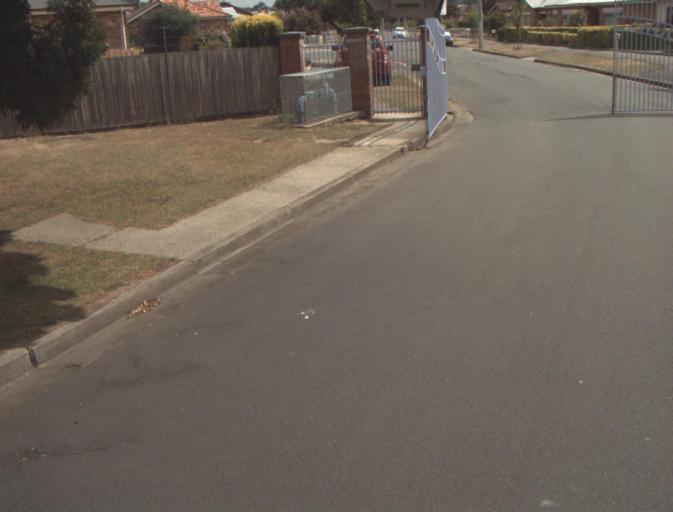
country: AU
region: Tasmania
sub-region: Launceston
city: Summerhill
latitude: -41.4723
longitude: 147.1598
